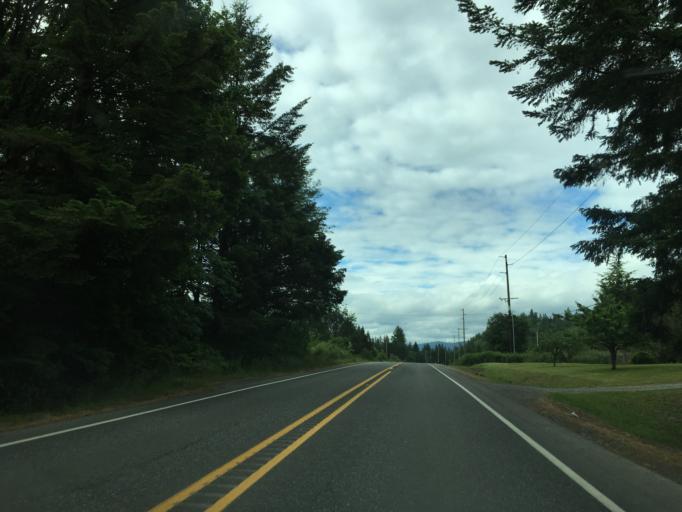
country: US
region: Washington
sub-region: Whatcom County
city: Peaceful Valley
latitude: 48.8450
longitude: -122.1638
